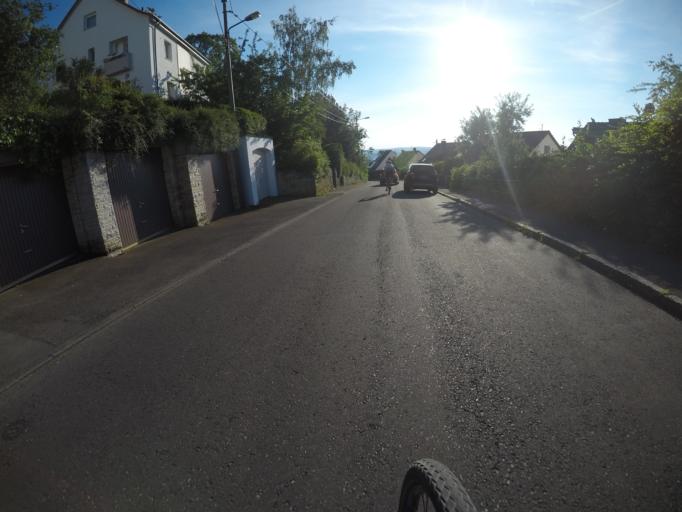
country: DE
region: Baden-Wuerttemberg
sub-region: Regierungsbezirk Stuttgart
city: Fellbach
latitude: 48.7838
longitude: 9.2770
